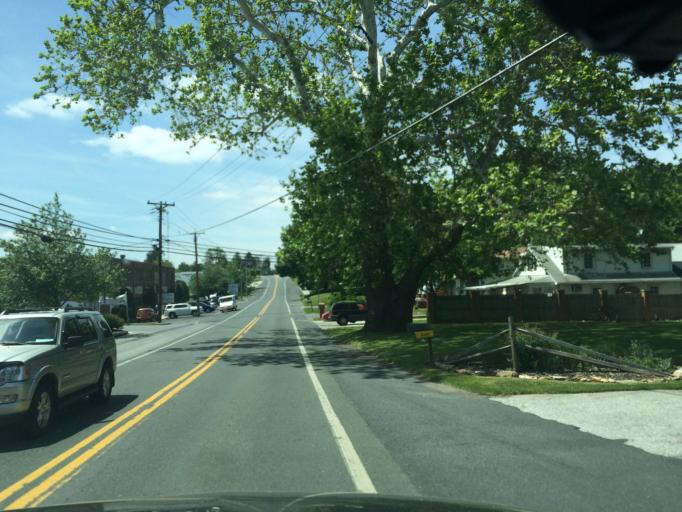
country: US
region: Maryland
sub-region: Carroll County
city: Westminster
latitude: 39.5603
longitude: -76.9762
